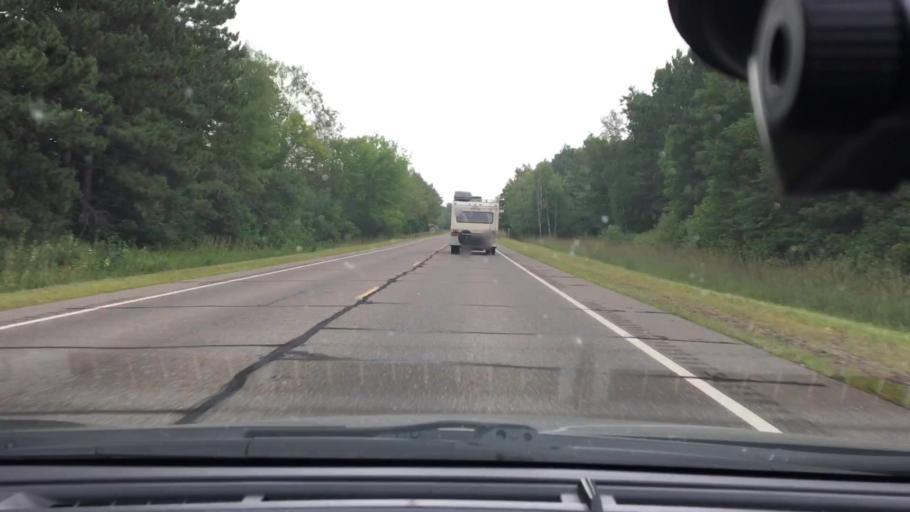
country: US
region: Minnesota
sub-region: Crow Wing County
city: Crosby
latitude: 46.4400
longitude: -93.8763
